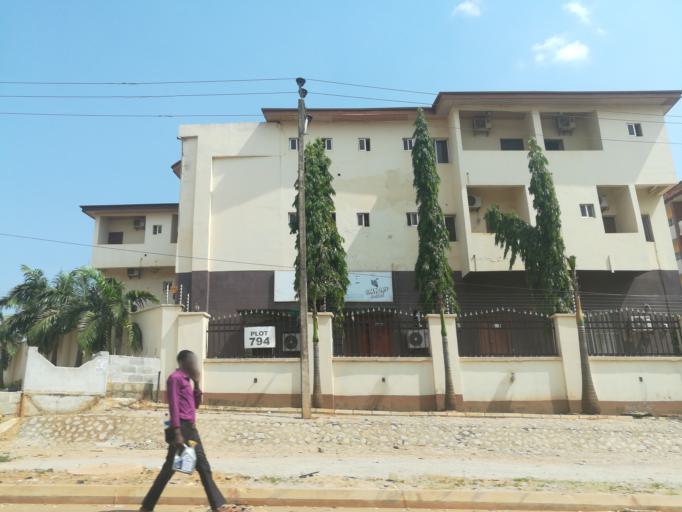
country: NG
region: Abuja Federal Capital Territory
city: Abuja
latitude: 9.0595
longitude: 7.4449
